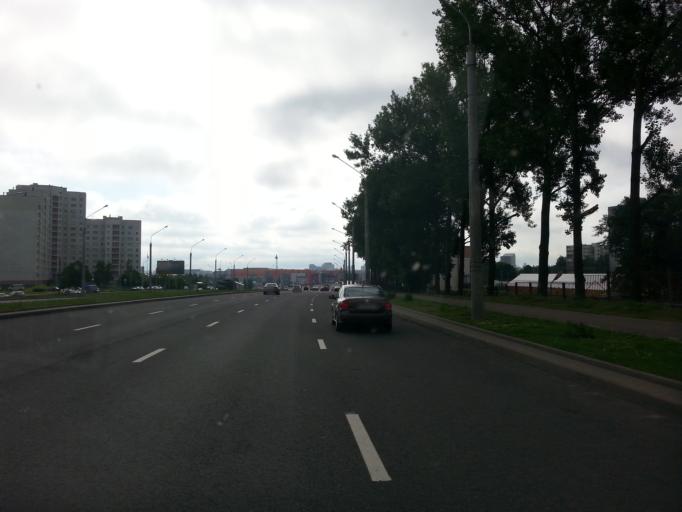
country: BY
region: Minsk
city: Novoye Medvezhino
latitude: 53.9295
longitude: 27.4969
